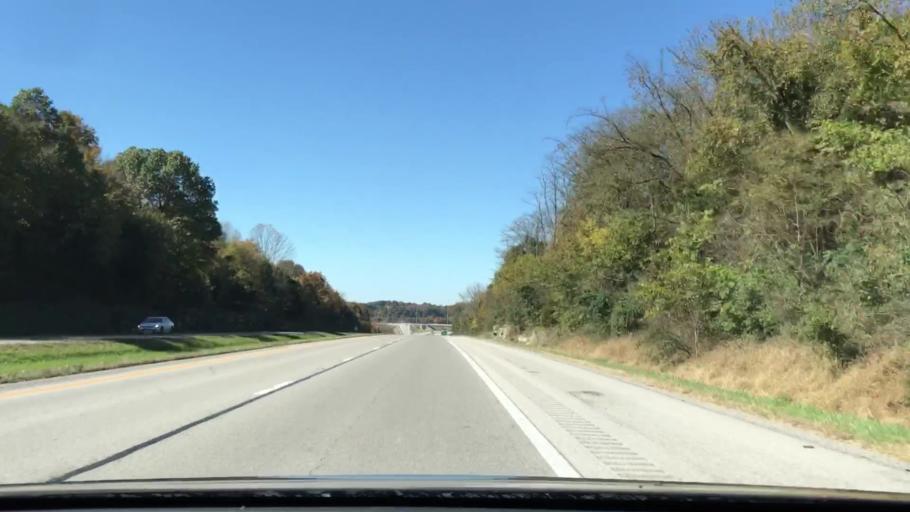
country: US
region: Kentucky
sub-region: Barren County
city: Glasgow
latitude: 36.9910
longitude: -85.9666
